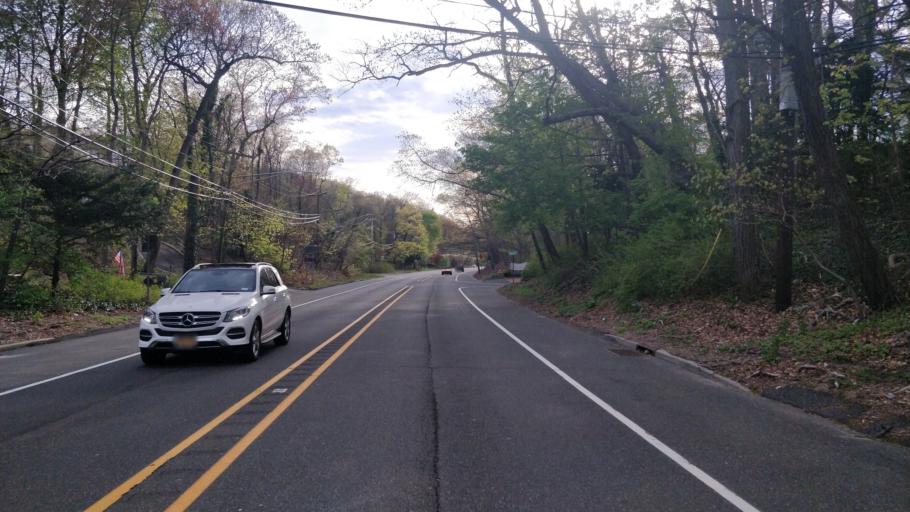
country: US
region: New York
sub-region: Suffolk County
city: Fort Salonga
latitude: 40.9130
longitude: -73.2905
